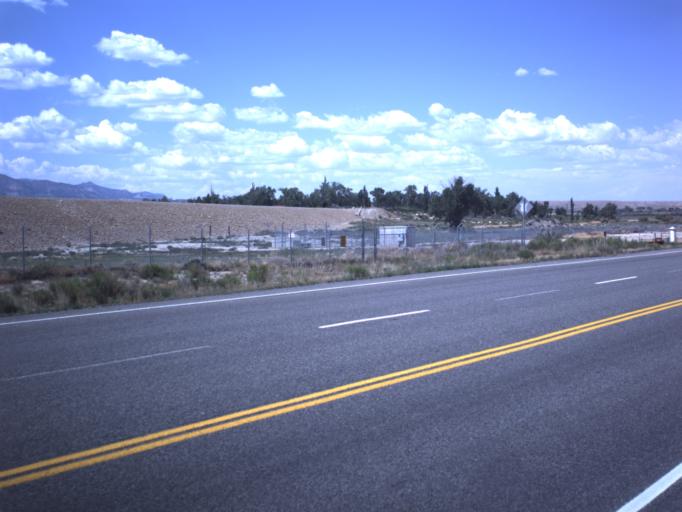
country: US
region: Utah
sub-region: Emery County
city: Huntington
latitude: 39.3416
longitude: -110.9415
